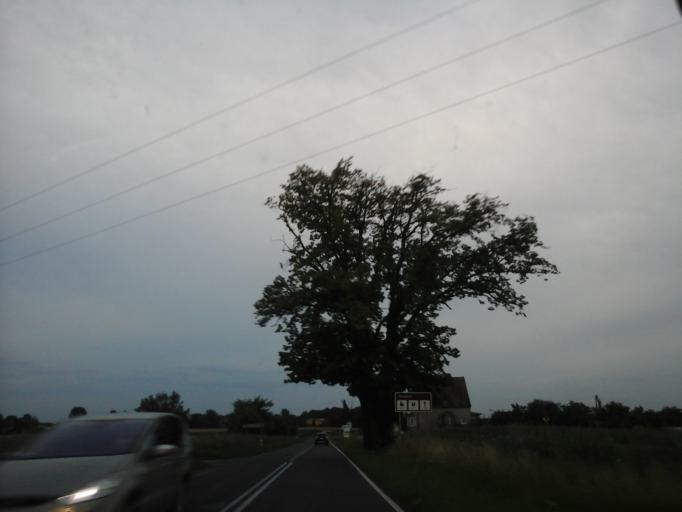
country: PL
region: West Pomeranian Voivodeship
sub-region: Powiat stargardzki
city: Stargard Szczecinski
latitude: 53.3543
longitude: 15.0608
